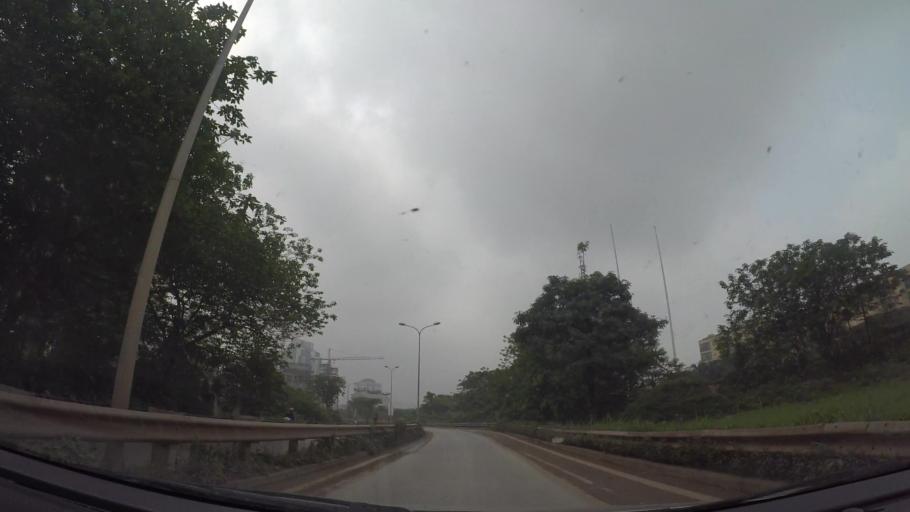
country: VN
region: Ha Noi
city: Tay Ho
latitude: 21.0838
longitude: 105.7882
